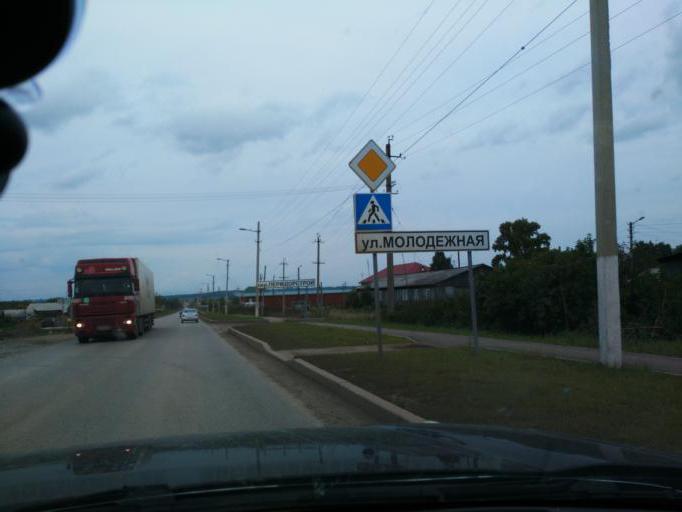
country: RU
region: Perm
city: Chernushka
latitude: 56.5350
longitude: 56.0974
